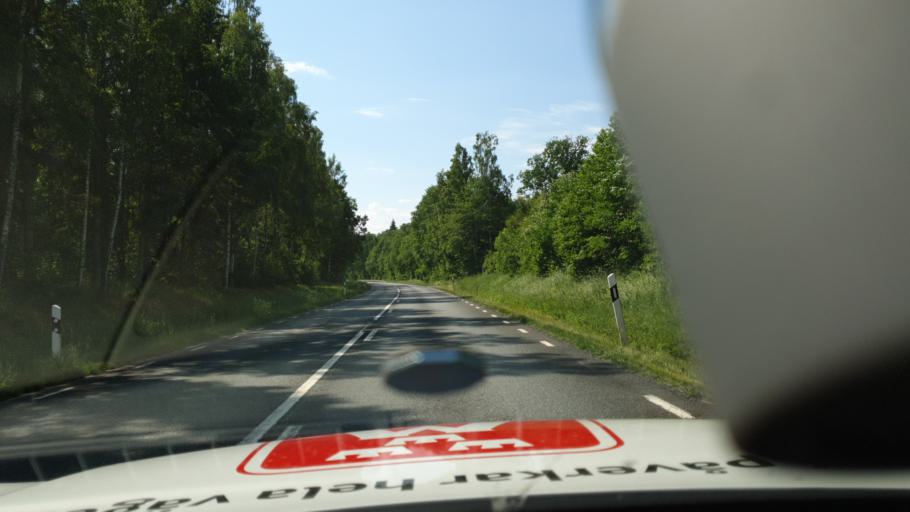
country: SE
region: Vaestra Goetaland
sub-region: Hjo Kommun
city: Hjo
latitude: 58.1129
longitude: 14.2092
